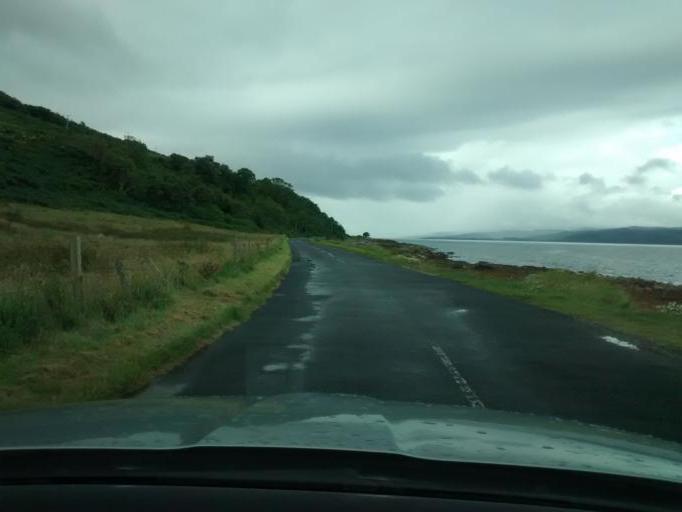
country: GB
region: Scotland
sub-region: North Ayrshire
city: Isle of Arran
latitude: 55.6666
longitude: -5.3731
